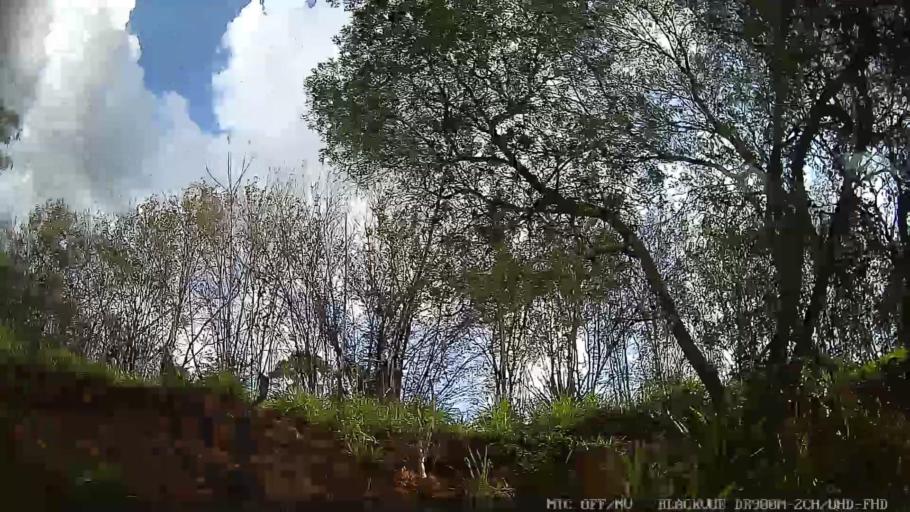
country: BR
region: Sao Paulo
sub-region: Braganca Paulista
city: Braganca Paulista
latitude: -22.9100
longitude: -46.4820
